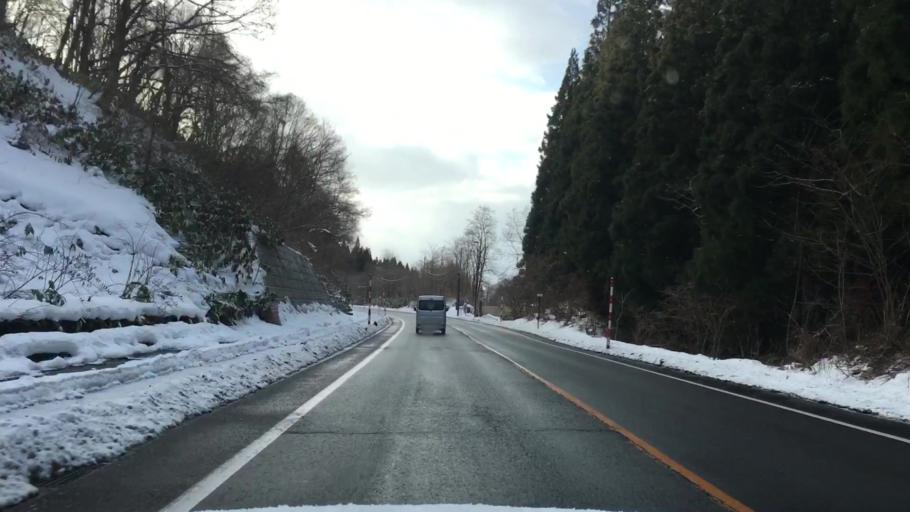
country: JP
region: Akita
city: Odate
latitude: 40.3928
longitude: 140.6051
